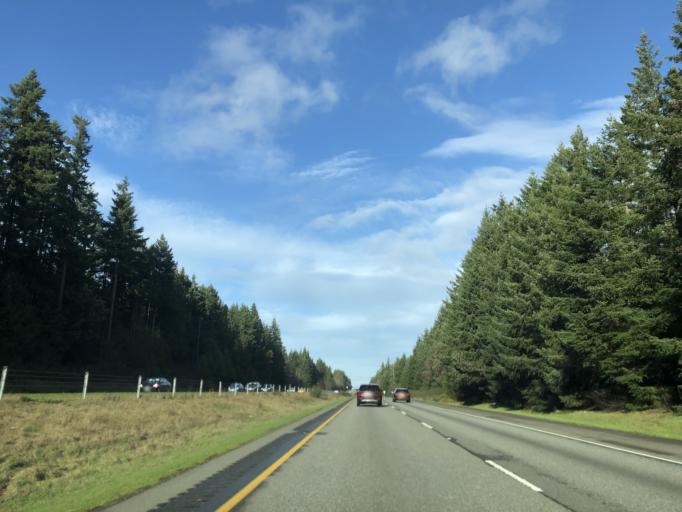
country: US
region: Washington
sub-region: Kitsap County
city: Bangor Trident Base
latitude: 47.7113
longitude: -122.6816
